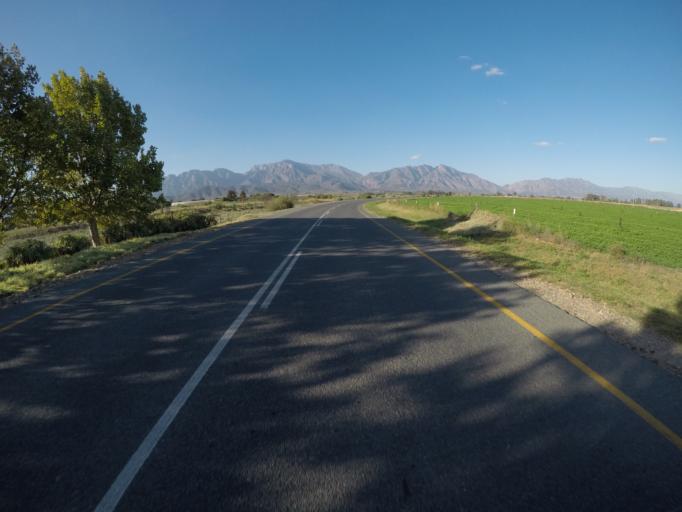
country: ZA
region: Western Cape
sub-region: Cape Winelands District Municipality
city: Worcester
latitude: -33.6755
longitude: 19.5310
